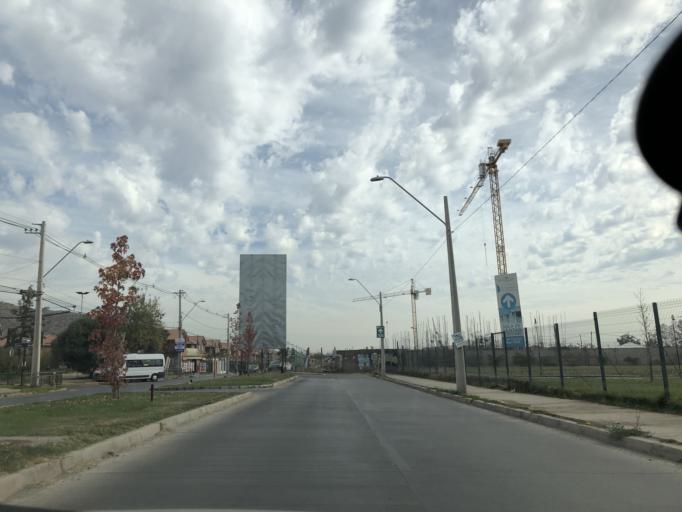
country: CL
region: Santiago Metropolitan
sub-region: Provincia de Cordillera
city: Puente Alto
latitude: -33.5953
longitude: -70.5482
